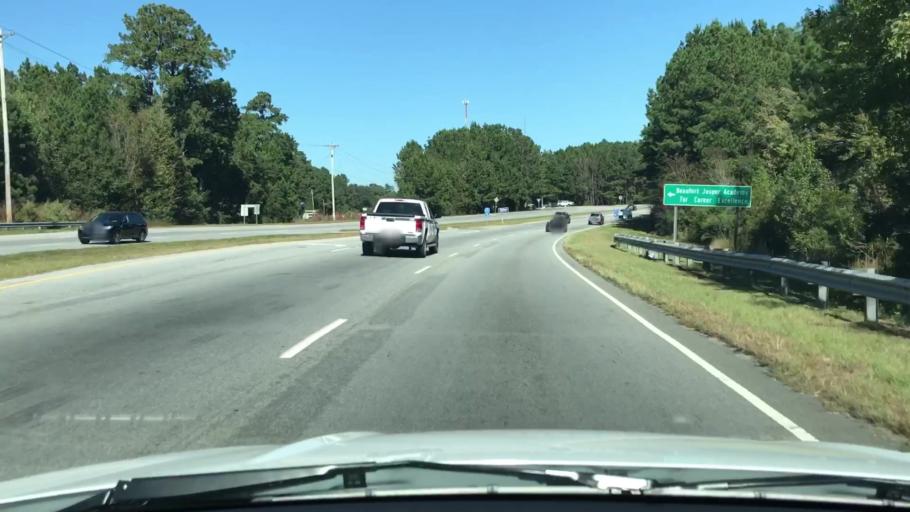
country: US
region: South Carolina
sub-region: Beaufort County
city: Bluffton
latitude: 32.3494
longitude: -80.9248
